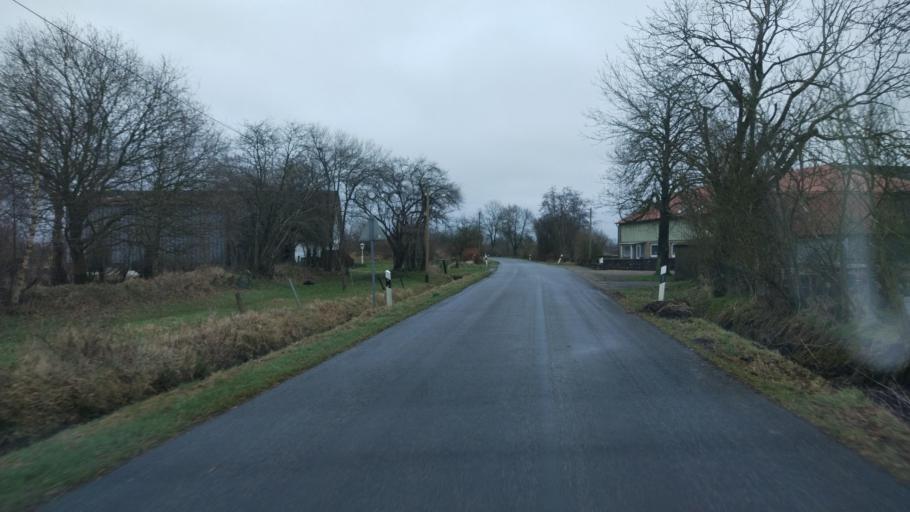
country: DE
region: Schleswig-Holstein
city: Hollingstedt
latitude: 54.4830
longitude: 9.3624
